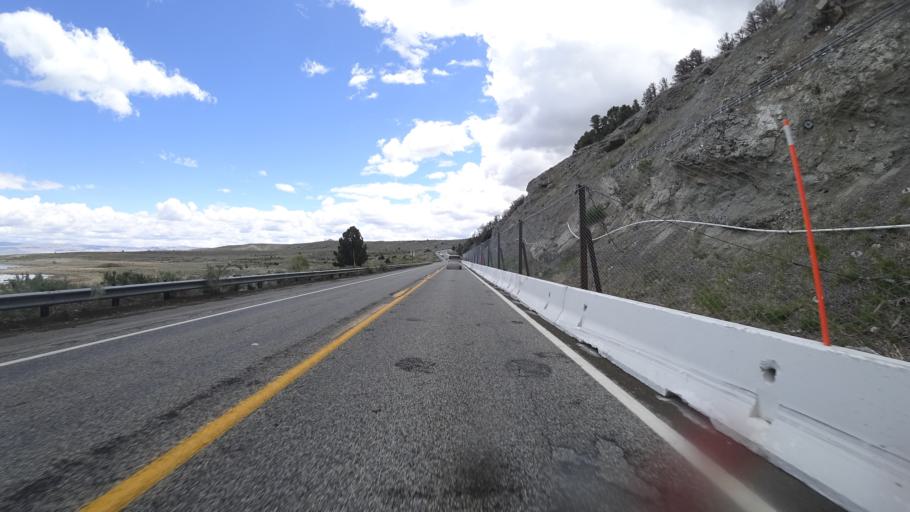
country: US
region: California
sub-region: Mono County
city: Bridgeport
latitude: 37.9781
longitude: -119.1367
